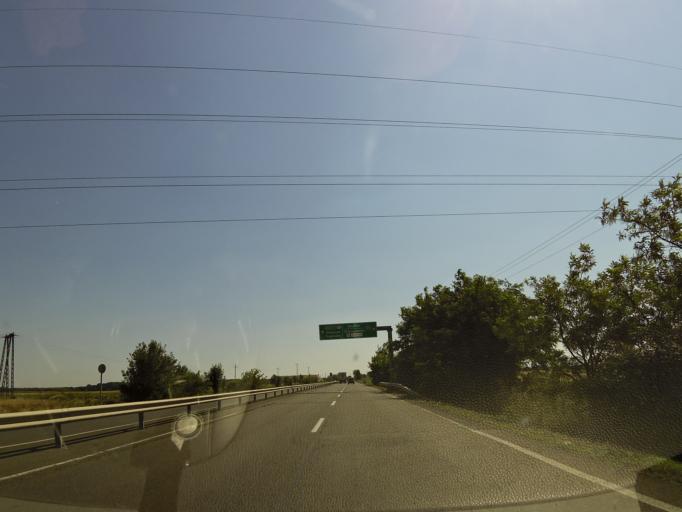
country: HU
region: Jasz-Nagykun-Szolnok
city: Tiszapuspoki
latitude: 47.1814
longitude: 20.3482
